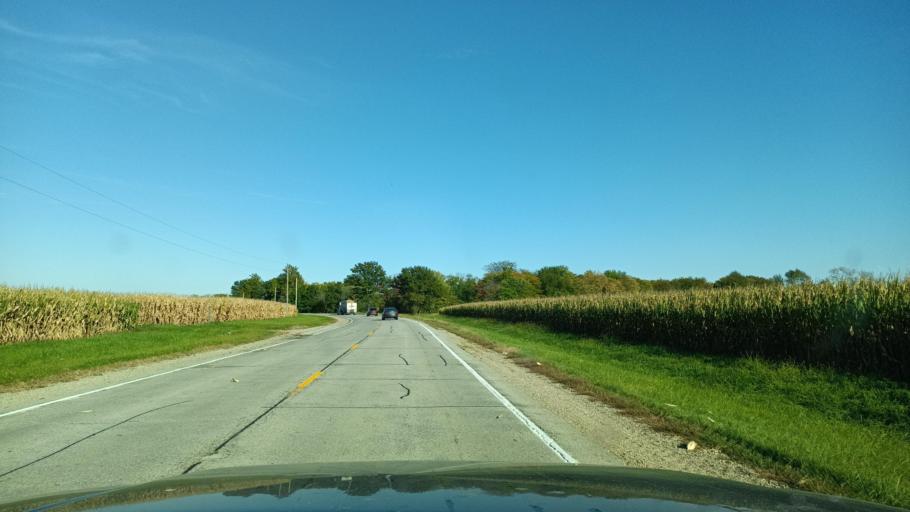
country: US
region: Illinois
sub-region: De Witt County
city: Farmer City
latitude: 40.2238
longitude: -88.6982
